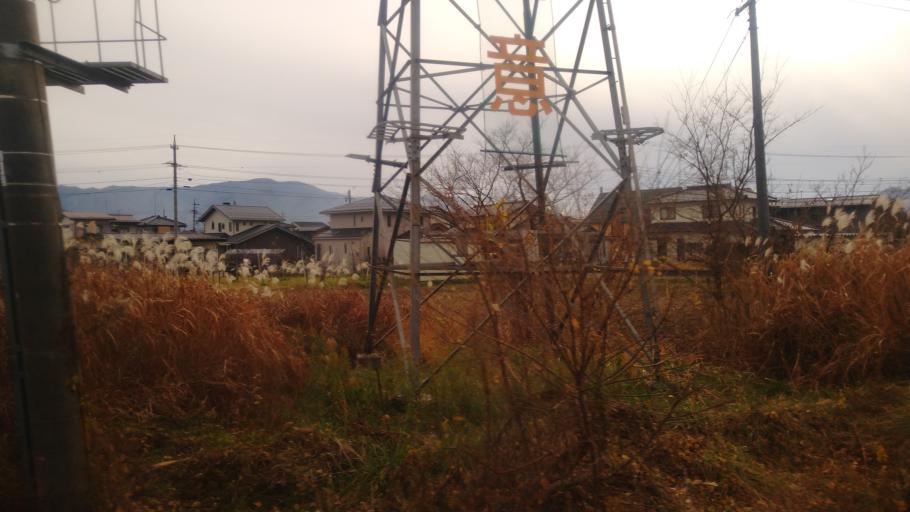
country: JP
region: Nagano
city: Nagano-shi
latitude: 36.5512
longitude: 138.1059
